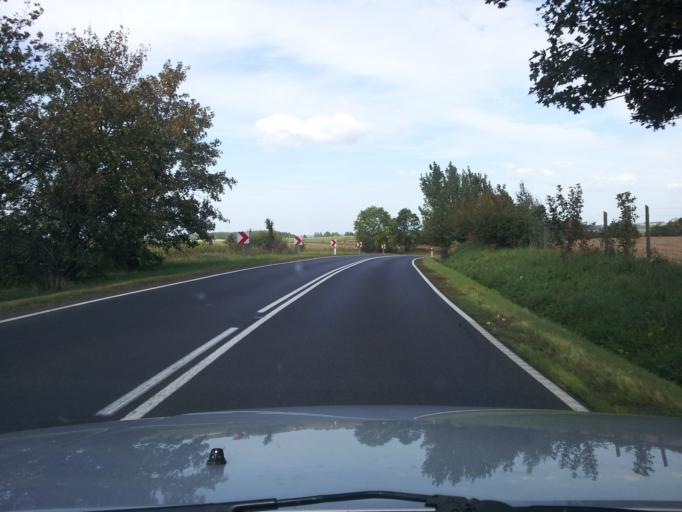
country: PL
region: Kujawsko-Pomorskie
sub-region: Powiat brodnicki
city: Brzozie
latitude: 53.3035
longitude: 19.5060
